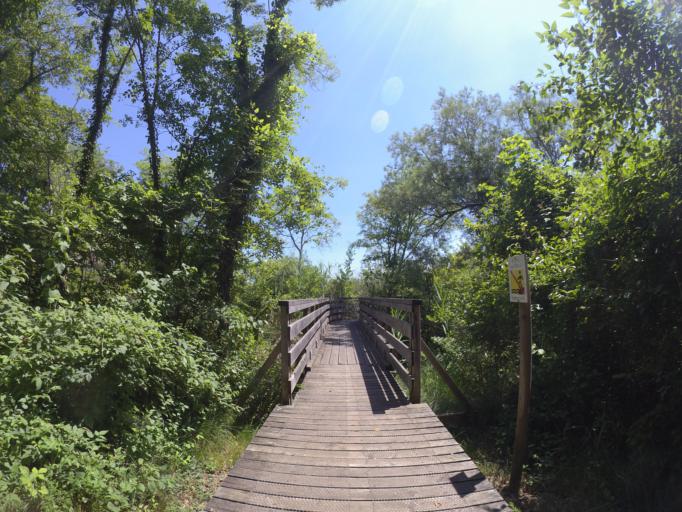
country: IT
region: Friuli Venezia Giulia
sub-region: Provincia di Udine
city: Bertiolo
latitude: 45.9194
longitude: 13.0756
